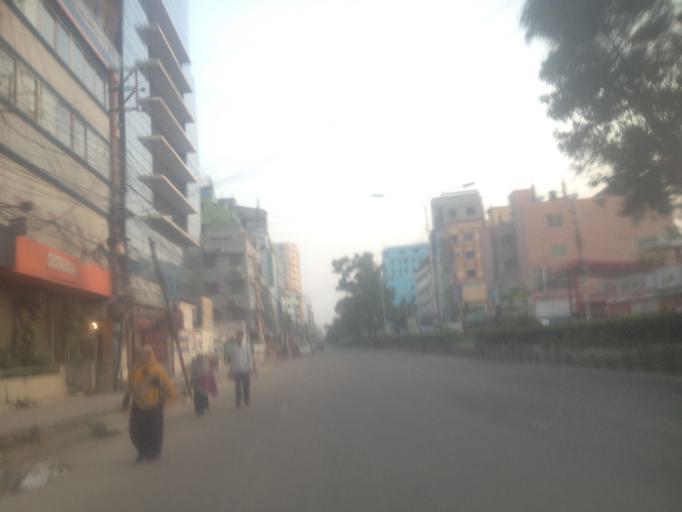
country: BD
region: Dhaka
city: Azimpur
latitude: 23.7856
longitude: 90.3777
